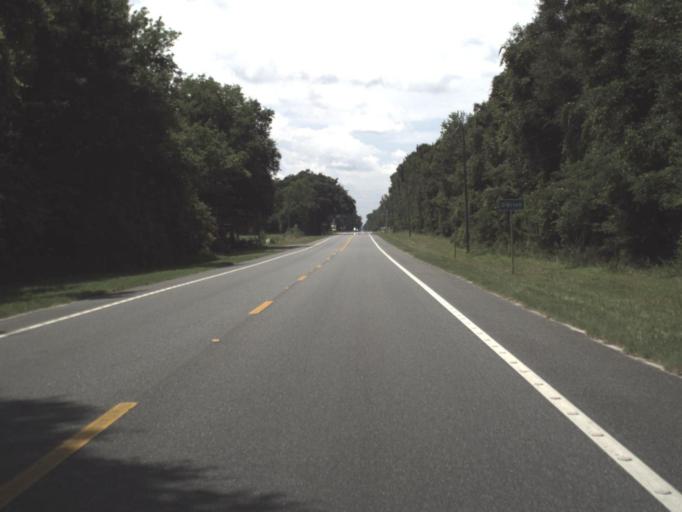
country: US
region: Florida
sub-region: Suwannee County
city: Wellborn
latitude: 30.0424
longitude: -82.9409
